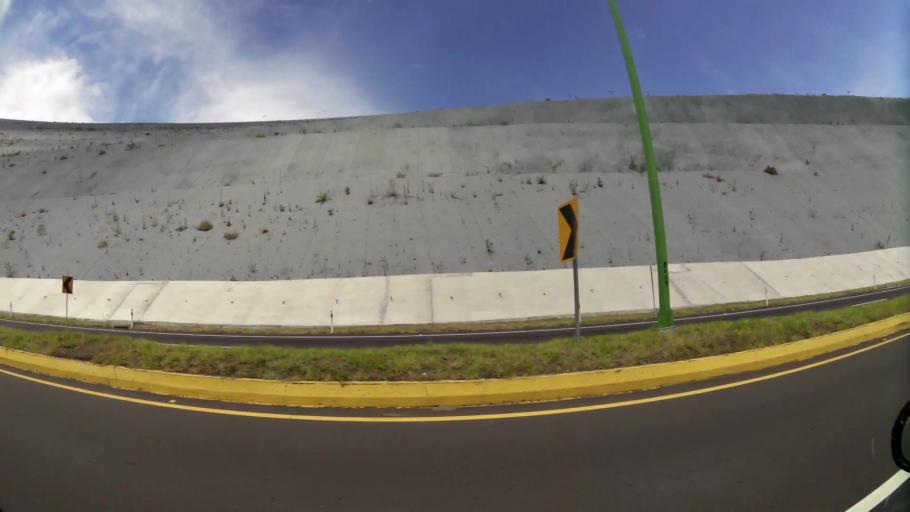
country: EC
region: Pichincha
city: Quito
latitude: -0.1048
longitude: -78.3766
